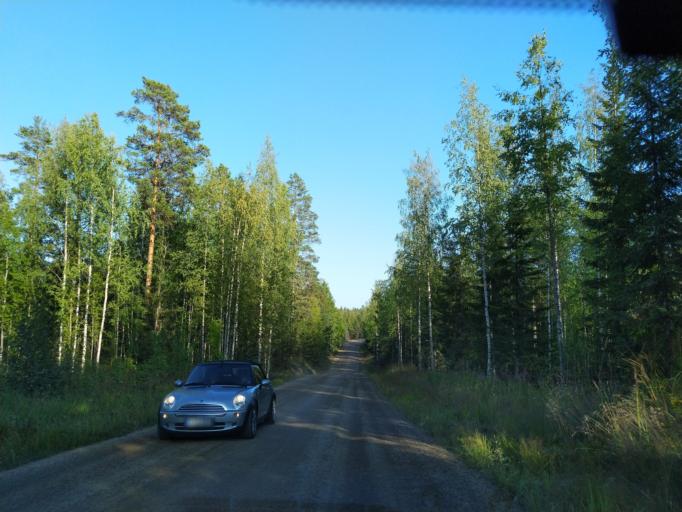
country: FI
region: Central Finland
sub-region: Jaemsae
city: Kuhmoinen
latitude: 61.6190
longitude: 25.1002
